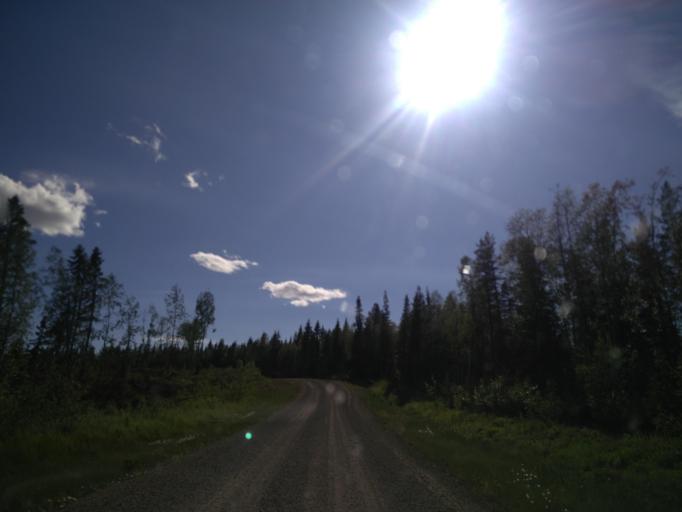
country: SE
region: Vaesternorrland
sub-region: Ange Kommun
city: Fransta
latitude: 62.2793
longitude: 16.3154
